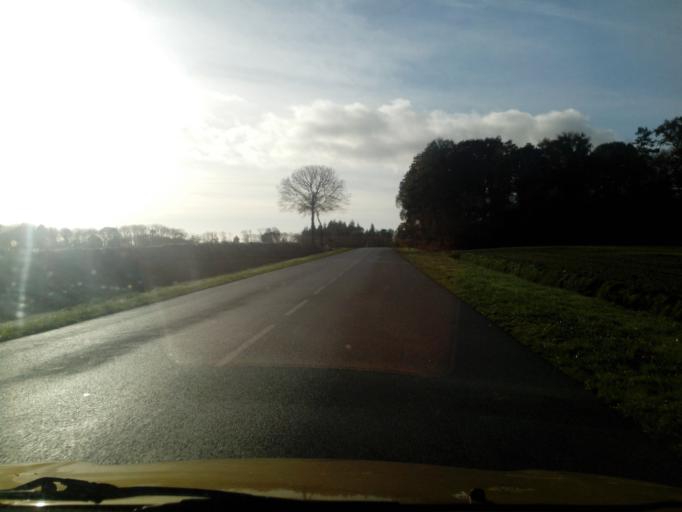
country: FR
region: Brittany
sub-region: Departement du Morbihan
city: Guilliers
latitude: 48.0606
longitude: -2.4130
